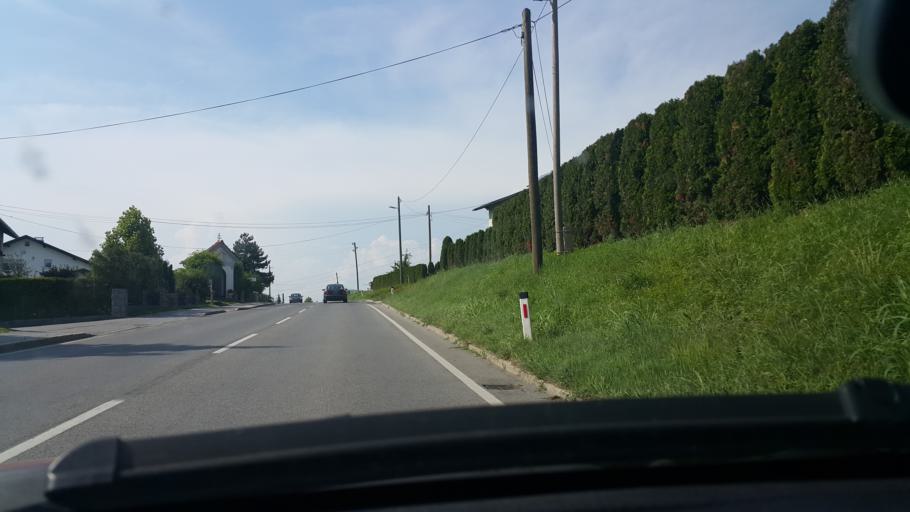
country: SI
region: Duplek
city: Zgornji Duplek
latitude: 46.5119
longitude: 15.7193
